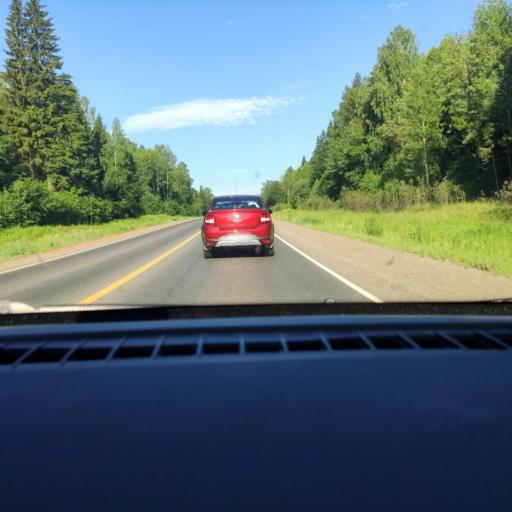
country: RU
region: Udmurtiya
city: Khokhryaki
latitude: 56.9159
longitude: 53.4319
